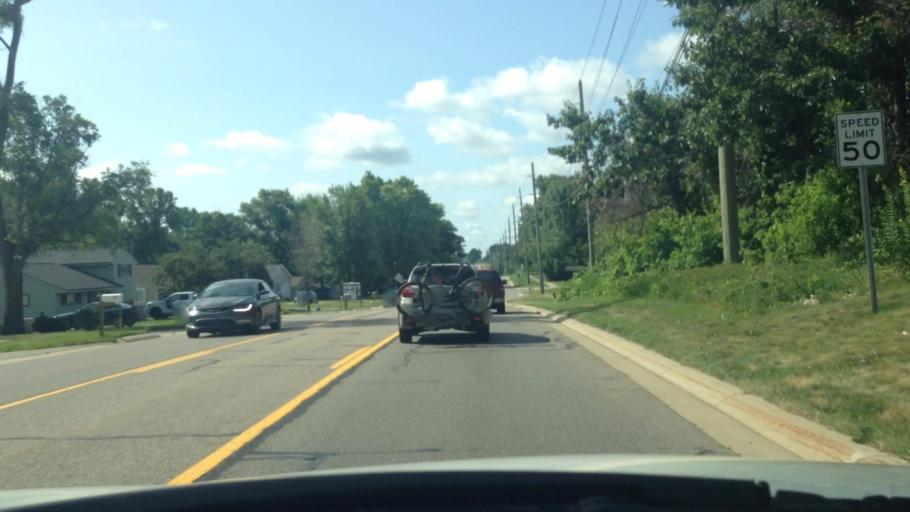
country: US
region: Michigan
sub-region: Oakland County
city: Waterford
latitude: 42.6400
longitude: -83.4432
